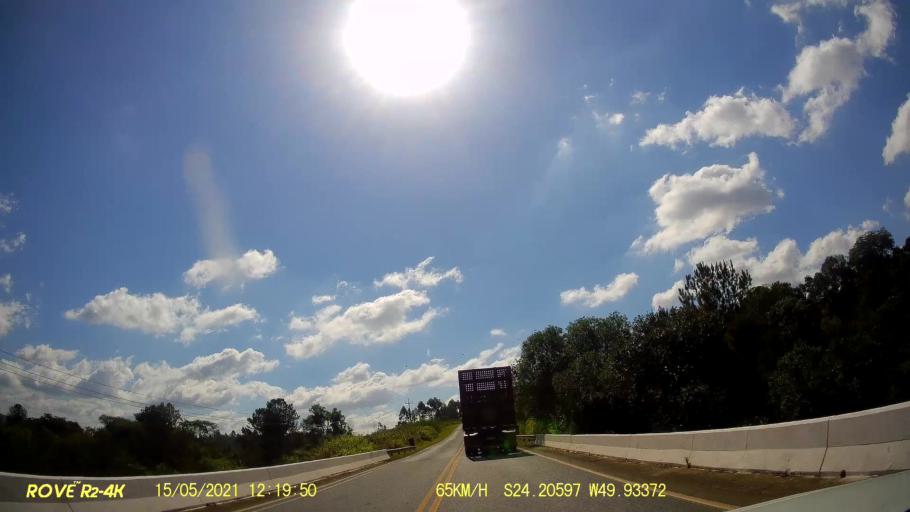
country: BR
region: Parana
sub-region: Jaguariaiva
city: Jaguariaiva
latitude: -24.2060
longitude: -49.9336
